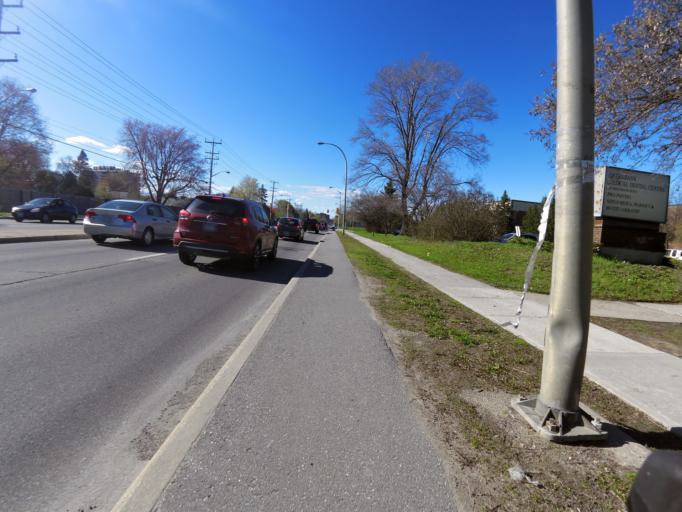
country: CA
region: Ontario
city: Bells Corners
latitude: 45.3310
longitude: -75.7821
